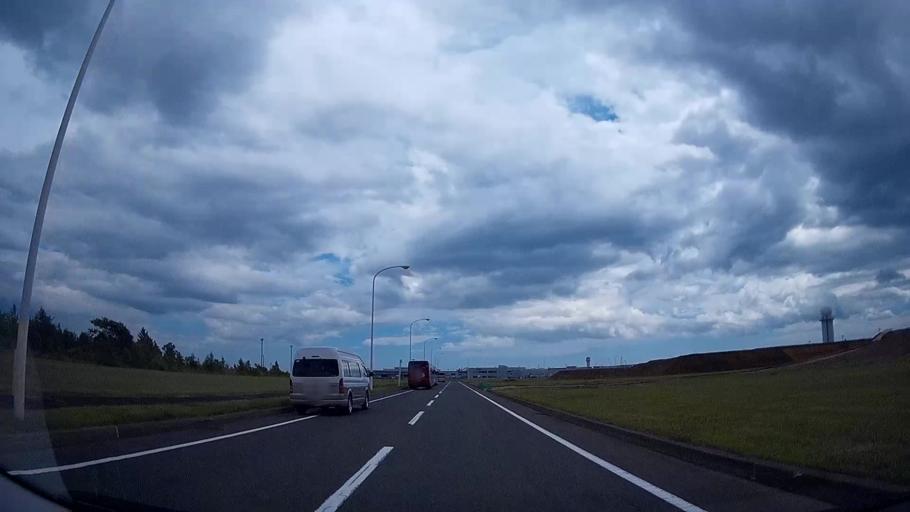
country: JP
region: Hokkaido
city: Chitose
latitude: 42.7997
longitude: 141.6800
